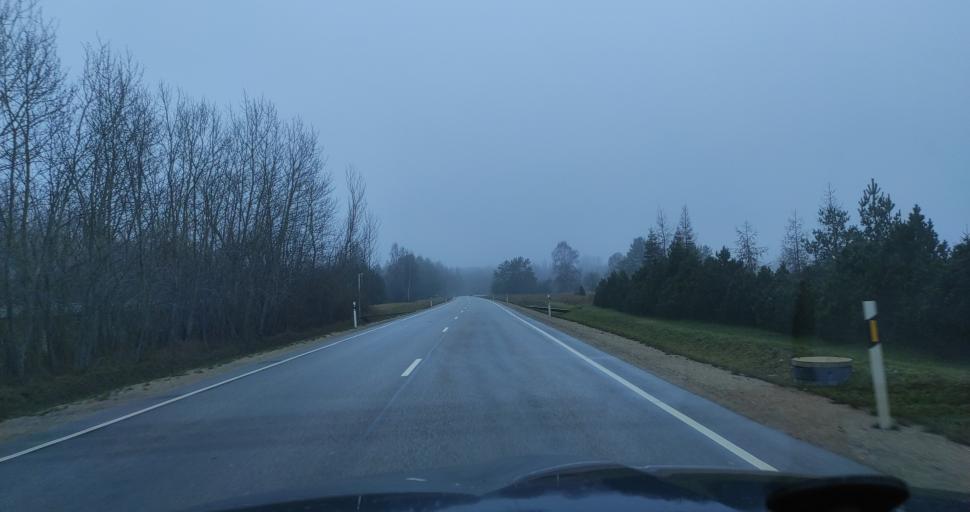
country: LV
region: Pavilostas
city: Pavilosta
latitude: 56.9269
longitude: 21.2677
